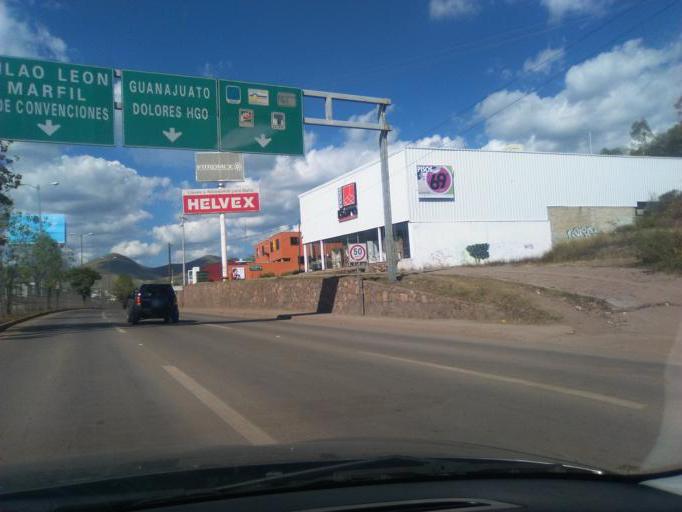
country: MX
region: Guanajuato
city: Marfil
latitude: 20.9900
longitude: -101.2852
